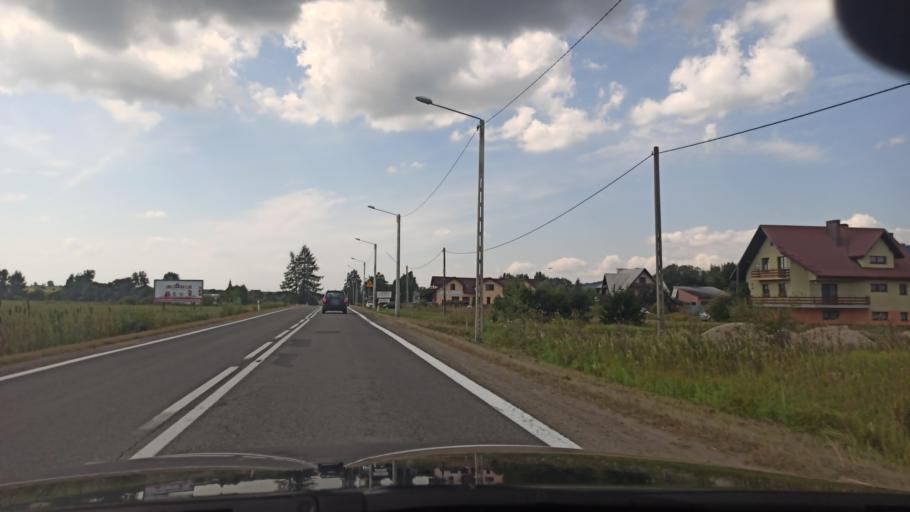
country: PL
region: Lesser Poland Voivodeship
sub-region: Powiat nowotarski
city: Lopuszna
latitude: 49.4725
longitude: 20.1178
